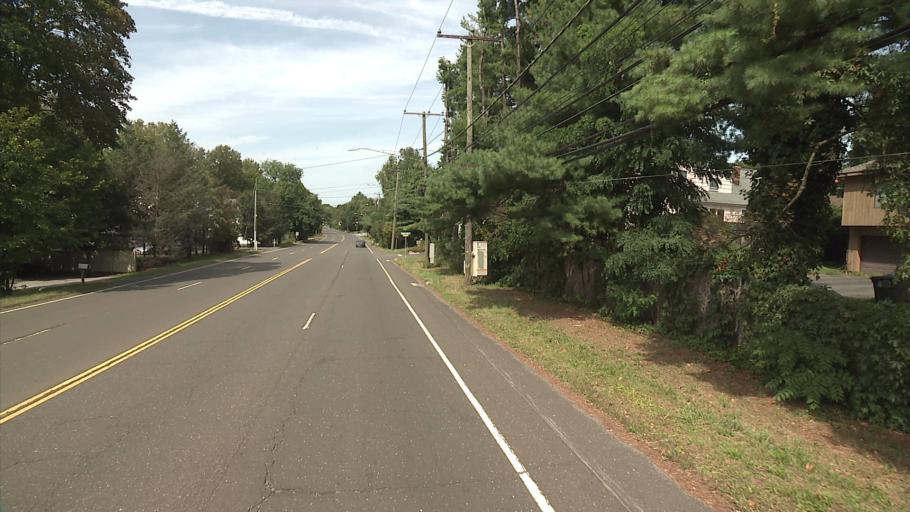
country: US
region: Connecticut
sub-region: Fairfield County
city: Stamford
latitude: 41.0832
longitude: -73.5546
